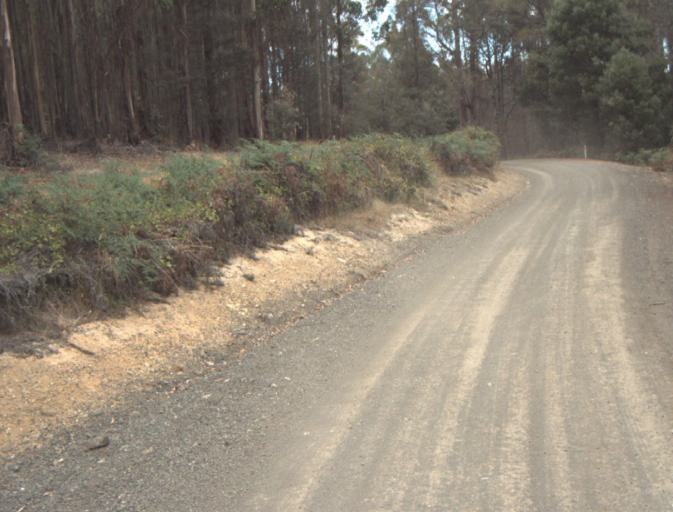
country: AU
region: Tasmania
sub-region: Launceston
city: Mayfield
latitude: -41.2137
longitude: 147.1778
